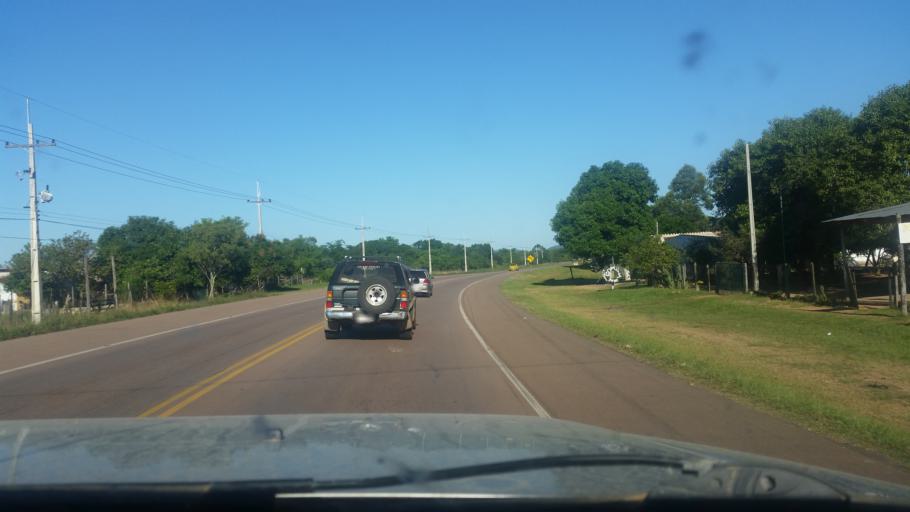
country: PY
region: Paraguari
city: Paraguari
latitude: -25.6317
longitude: -57.0670
